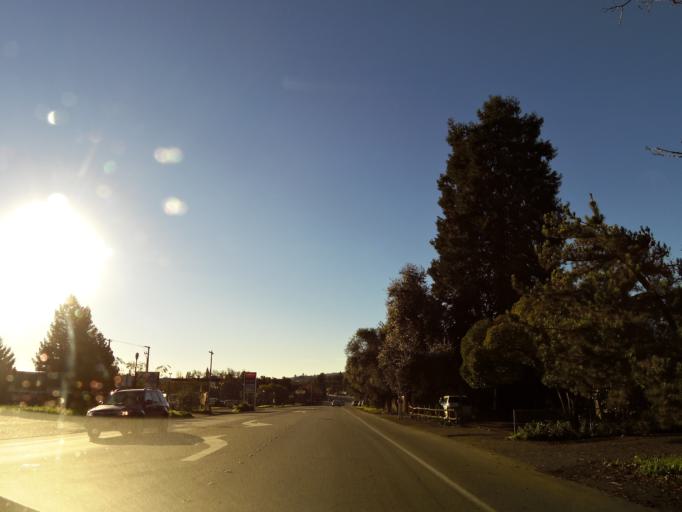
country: US
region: California
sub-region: Sonoma County
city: Cloverdale
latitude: 38.7940
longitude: -123.0182
